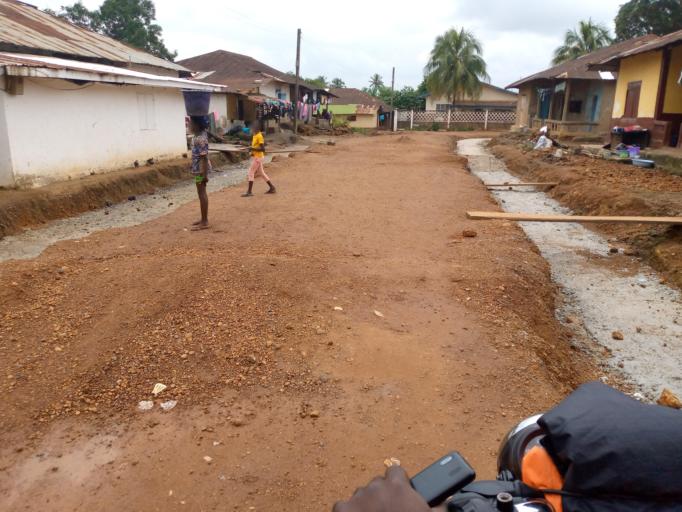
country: SL
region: Eastern Province
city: Kenema
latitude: 7.8740
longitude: -11.1876
